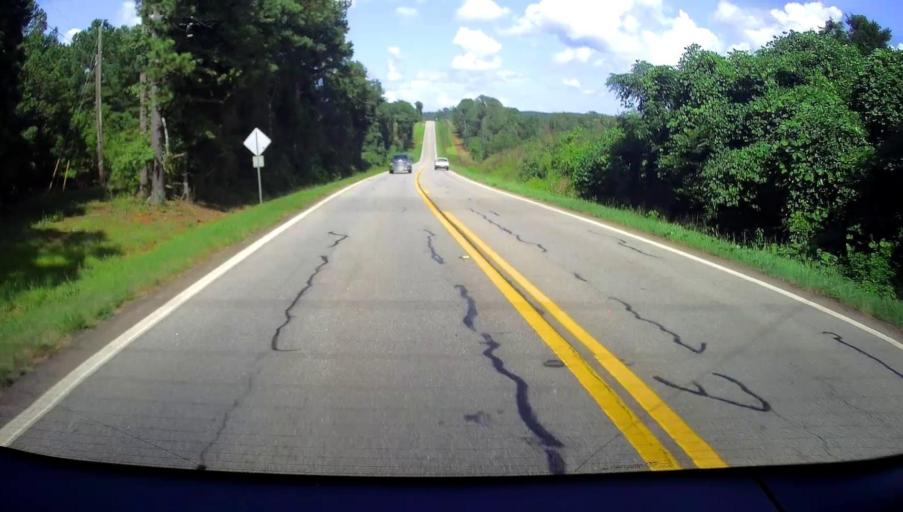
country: US
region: Georgia
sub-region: Upson County
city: Thomaston
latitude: 32.9150
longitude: -84.2598
